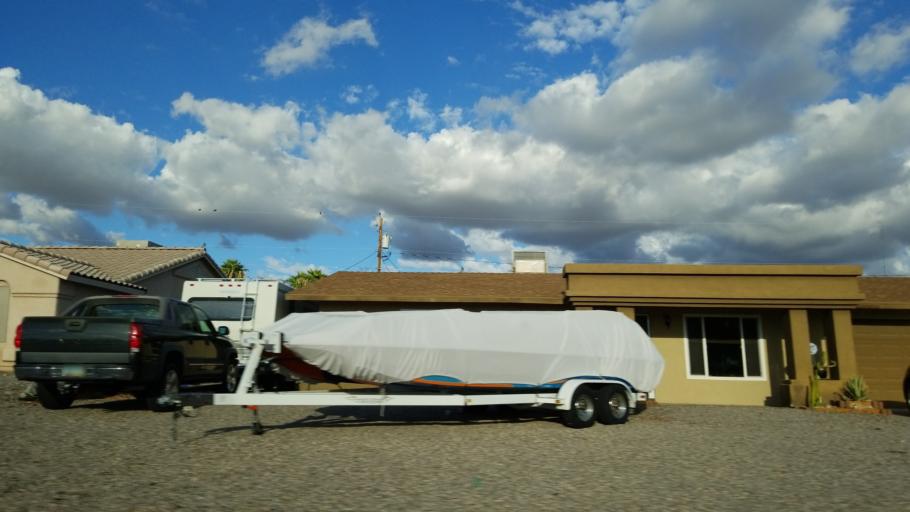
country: US
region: Arizona
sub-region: Mohave County
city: Lake Havasu City
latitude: 34.4606
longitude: -114.2588
